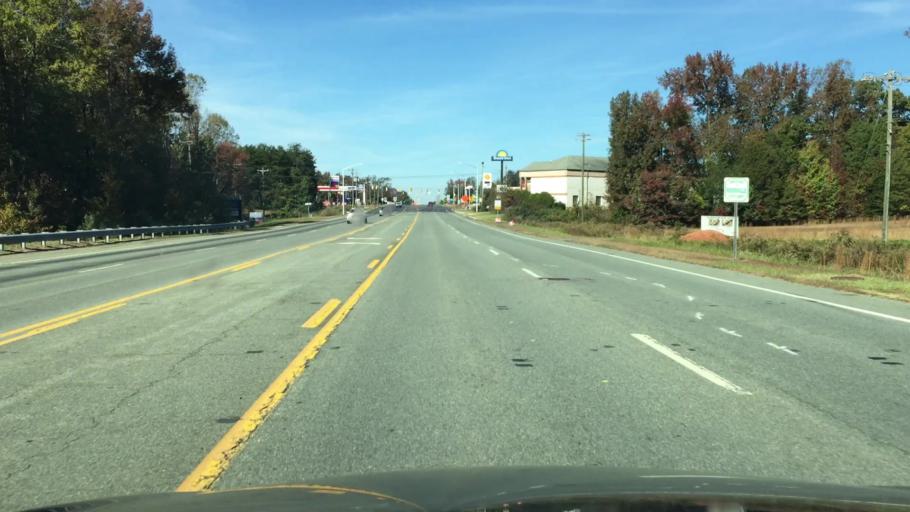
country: US
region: North Carolina
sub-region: Rockingham County
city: Reidsville
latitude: 36.3239
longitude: -79.6379
